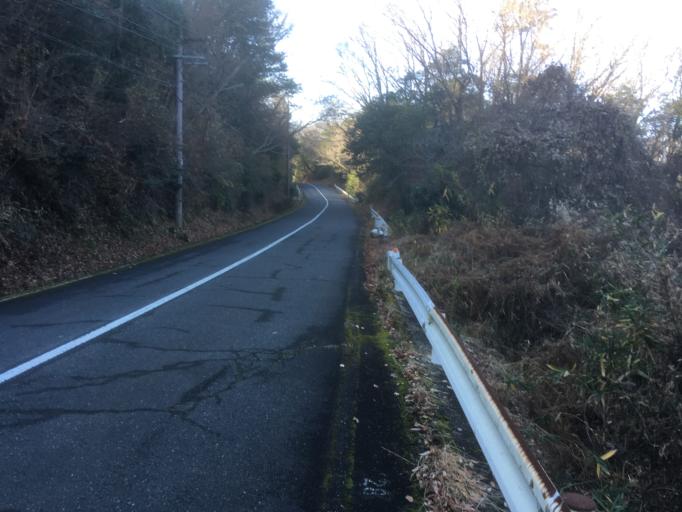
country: JP
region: Nara
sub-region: Ikoma-shi
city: Ikoma
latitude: 34.6937
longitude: 135.6782
